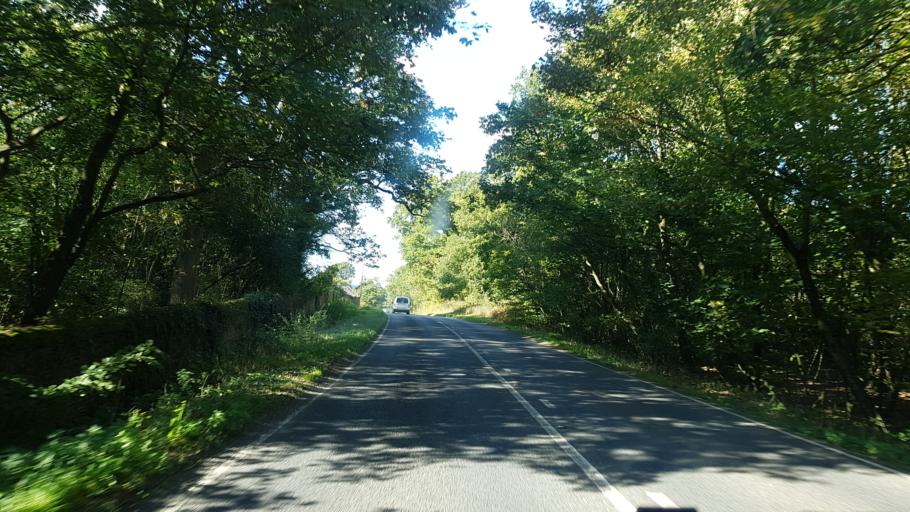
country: GB
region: England
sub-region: West Sussex
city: Petworth
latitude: 51.0351
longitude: -0.6353
